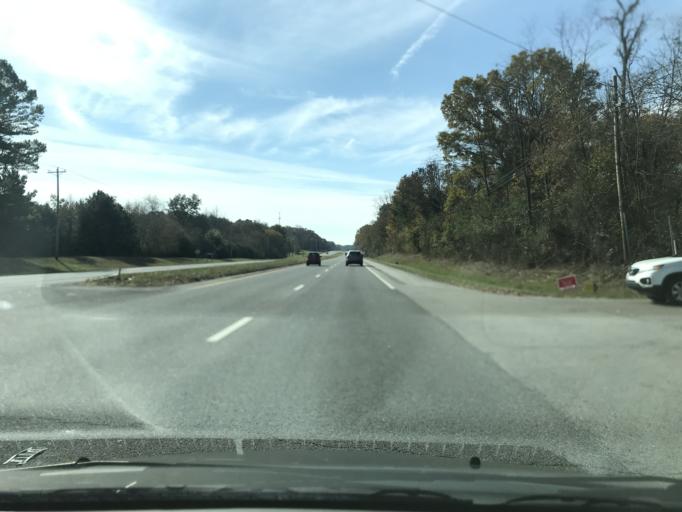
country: US
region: Tennessee
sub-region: Coffee County
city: Manchester
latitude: 35.4265
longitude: -86.1096
